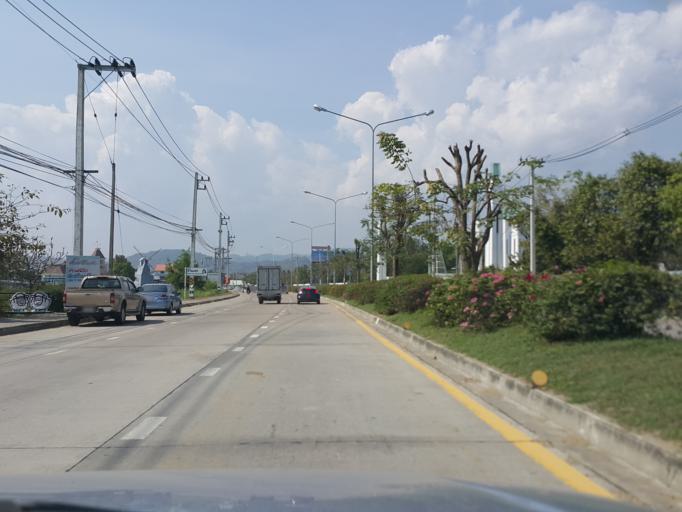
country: TH
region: Chiang Mai
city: Chiang Mai
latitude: 18.7476
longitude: 98.9502
